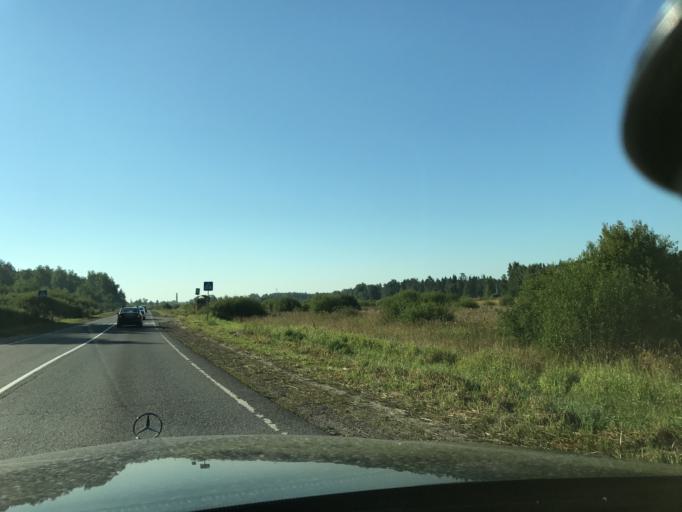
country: RU
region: Moskovskaya
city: Bakhchivandzhi
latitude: 55.8554
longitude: 38.0707
